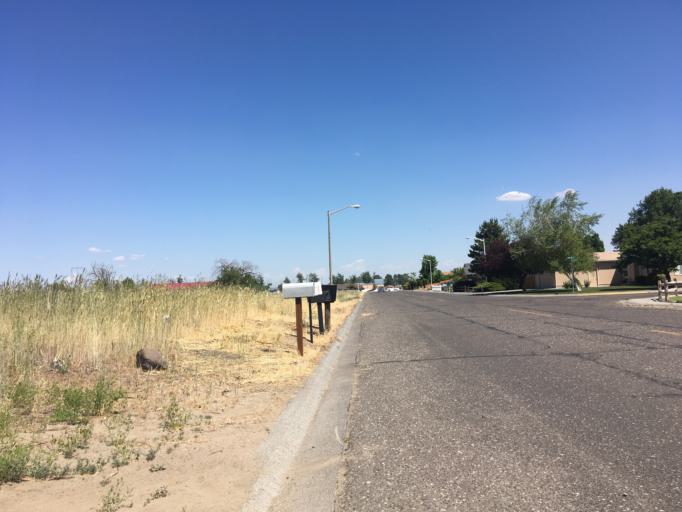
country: US
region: Oregon
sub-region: Morrow County
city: Boardman
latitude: 45.8317
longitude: -119.7071
